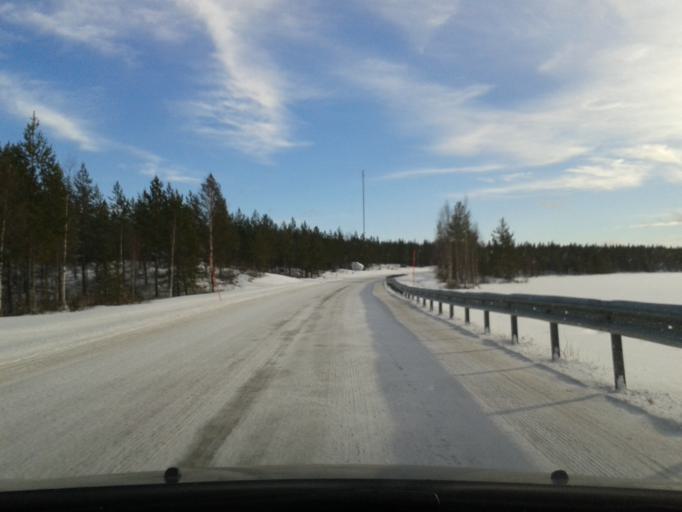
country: SE
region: Vaesterbotten
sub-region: Asele Kommun
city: Asele
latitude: 64.3030
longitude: 17.2553
